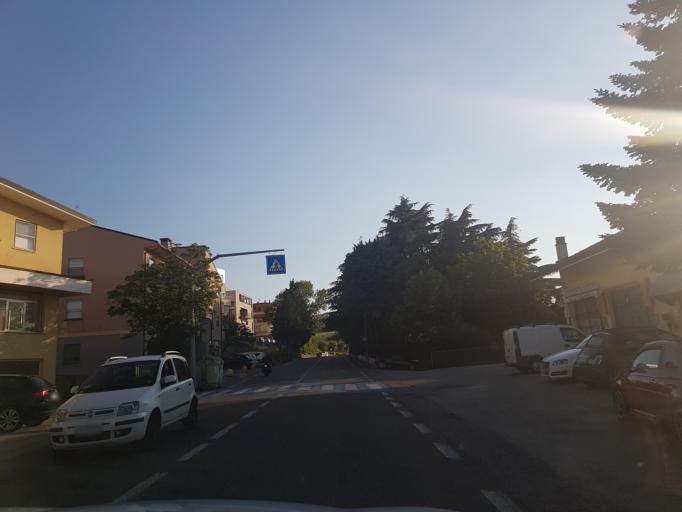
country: SM
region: Domagnano
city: Domagnano
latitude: 43.9571
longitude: 12.4676
